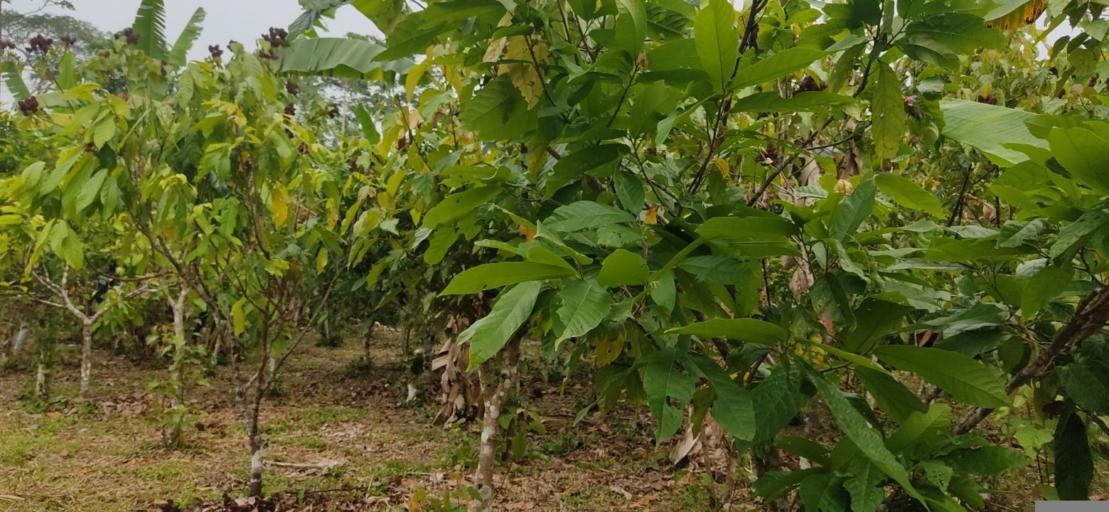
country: BO
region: La Paz
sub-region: Provincia Larecaja
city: Guanay
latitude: -15.5639
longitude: -67.3185
